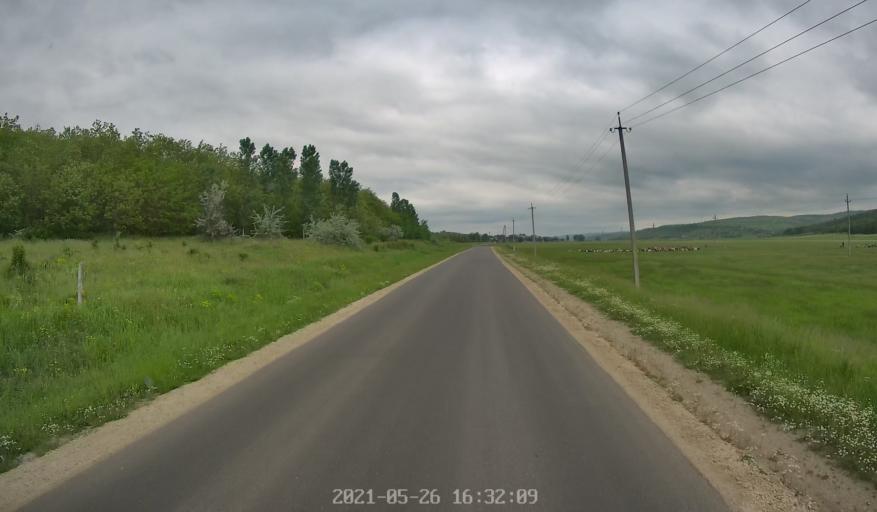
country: MD
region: Hincesti
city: Dancu
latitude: 46.8135
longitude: 28.3595
